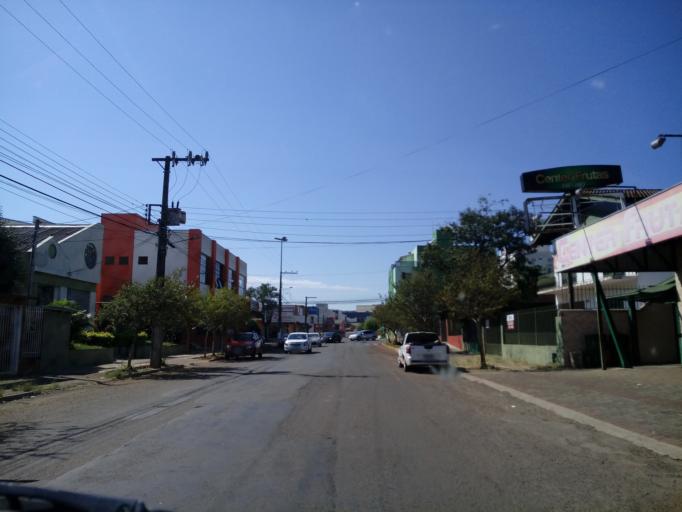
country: BR
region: Santa Catarina
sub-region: Chapeco
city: Chapeco
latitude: -27.0876
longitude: -52.6177
